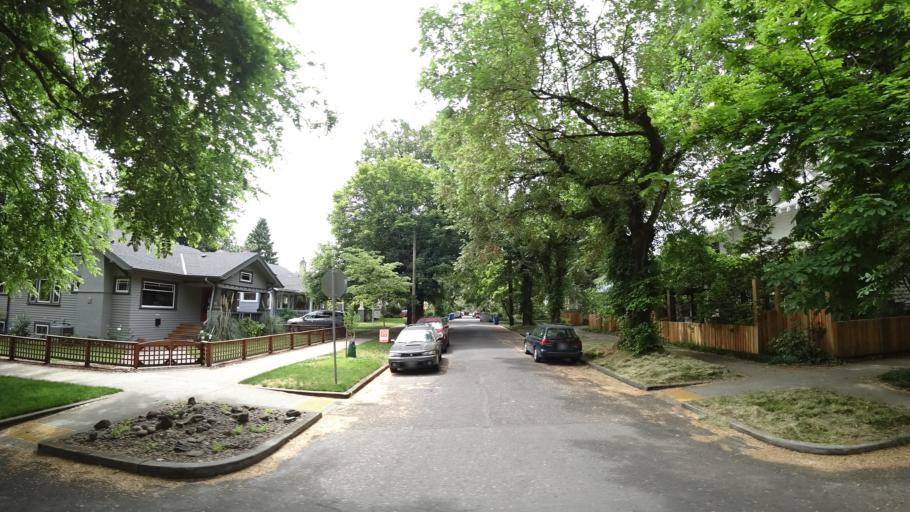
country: US
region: Oregon
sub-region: Multnomah County
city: Portland
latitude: 45.5365
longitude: -122.6099
